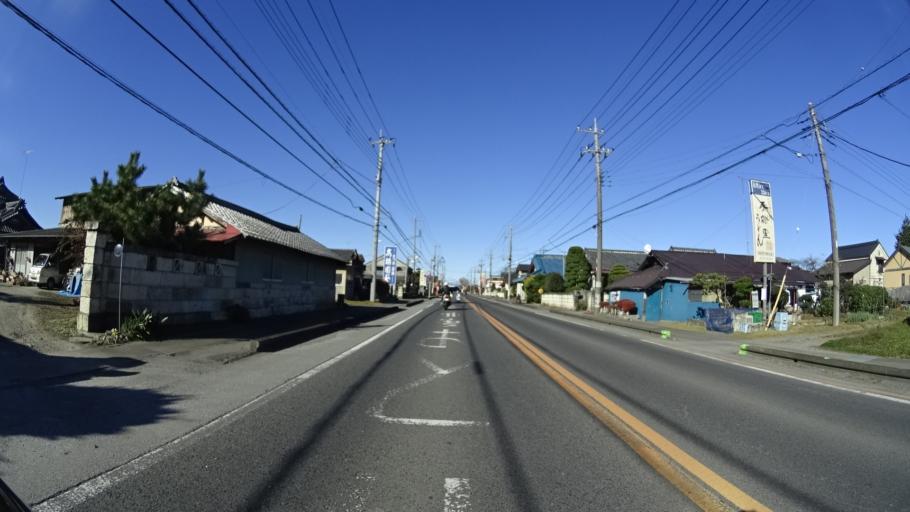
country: JP
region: Tochigi
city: Kanuma
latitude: 36.5177
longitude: 139.7517
